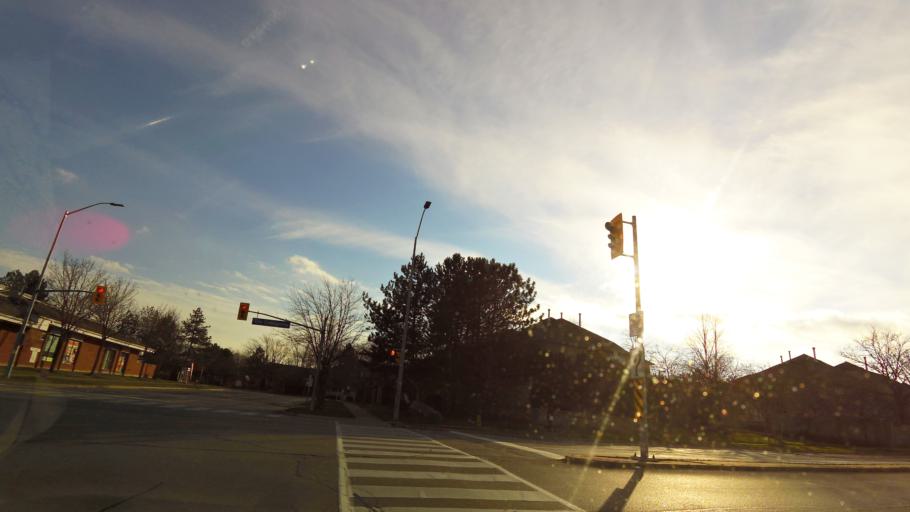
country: CA
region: Ontario
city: Mississauga
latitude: 43.5454
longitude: -79.6774
